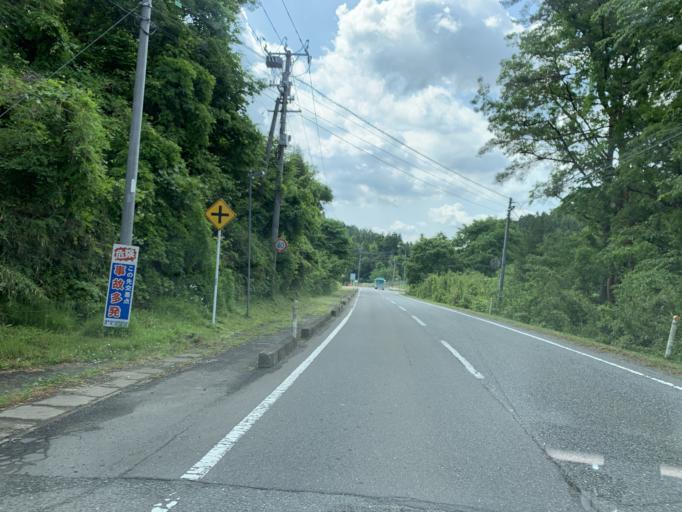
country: JP
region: Miyagi
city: Furukawa
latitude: 38.7740
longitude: 140.9614
